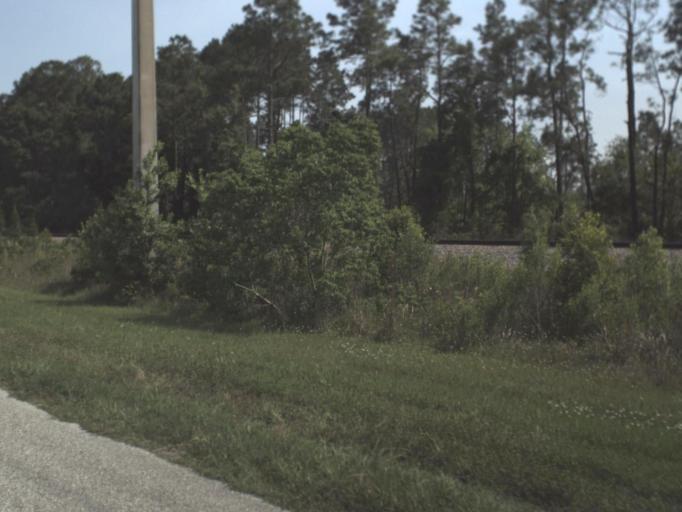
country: US
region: Florida
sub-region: Saint Johns County
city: Villano Beach
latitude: 29.9875
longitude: -81.3697
